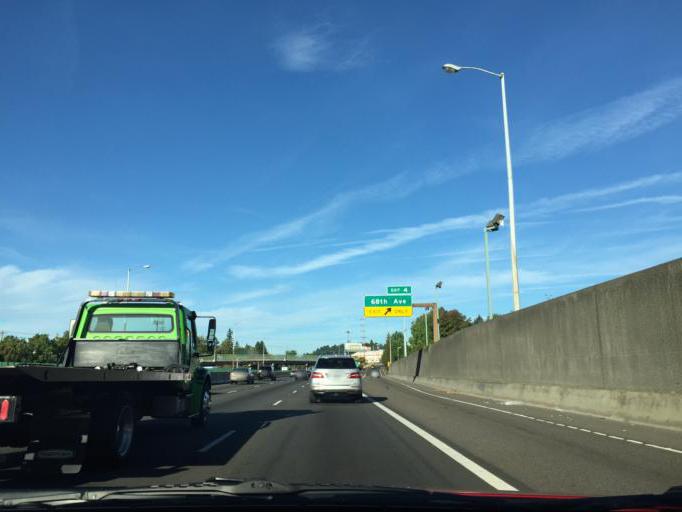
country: US
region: Oregon
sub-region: Multnomah County
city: Lents
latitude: 45.5318
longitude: -122.5963
